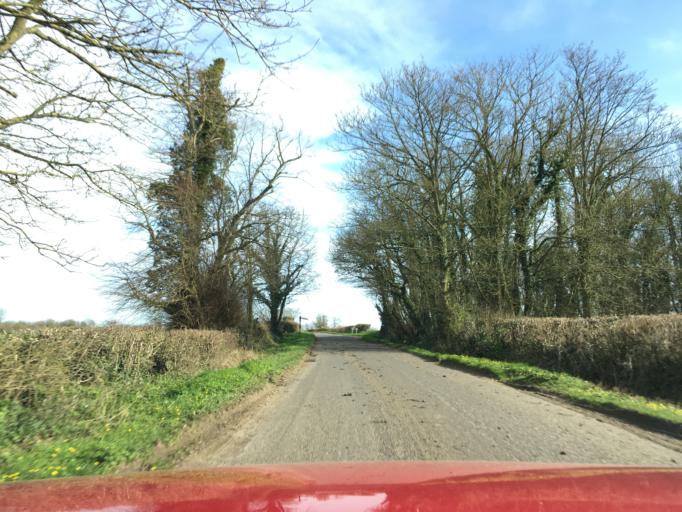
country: GB
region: England
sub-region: Wiltshire
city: Luckington
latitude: 51.5434
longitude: -2.2231
